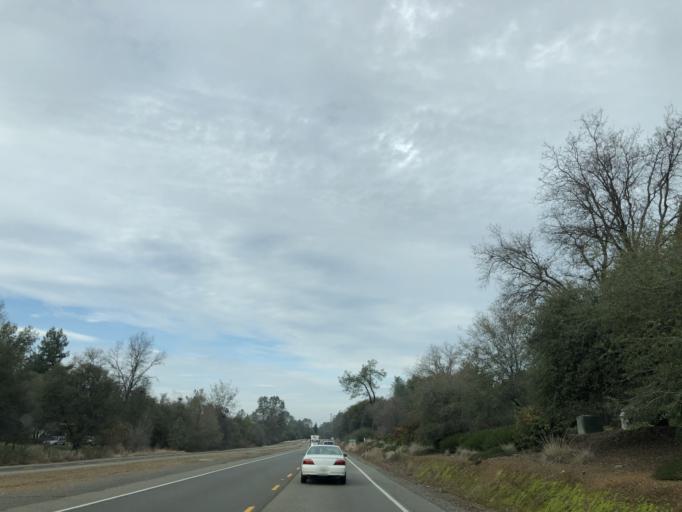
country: US
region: California
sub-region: El Dorado County
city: El Dorado Hills
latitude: 38.6943
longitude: -121.0821
